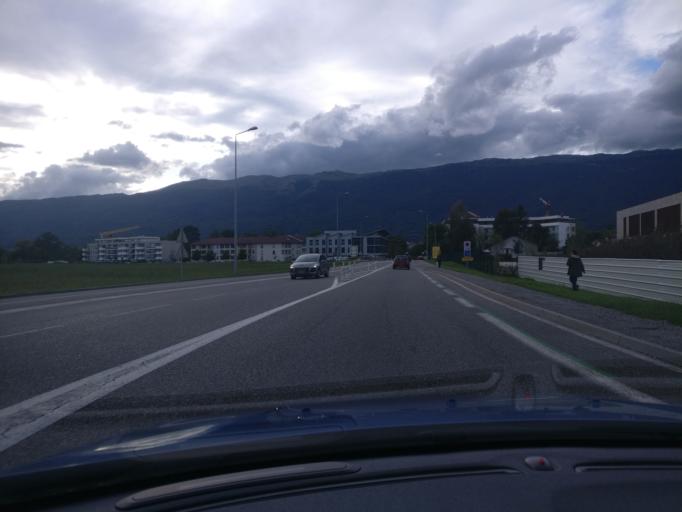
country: FR
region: Rhone-Alpes
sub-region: Departement de l'Ain
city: Saint-Genis-Pouilly
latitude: 46.2401
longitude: 6.0324
